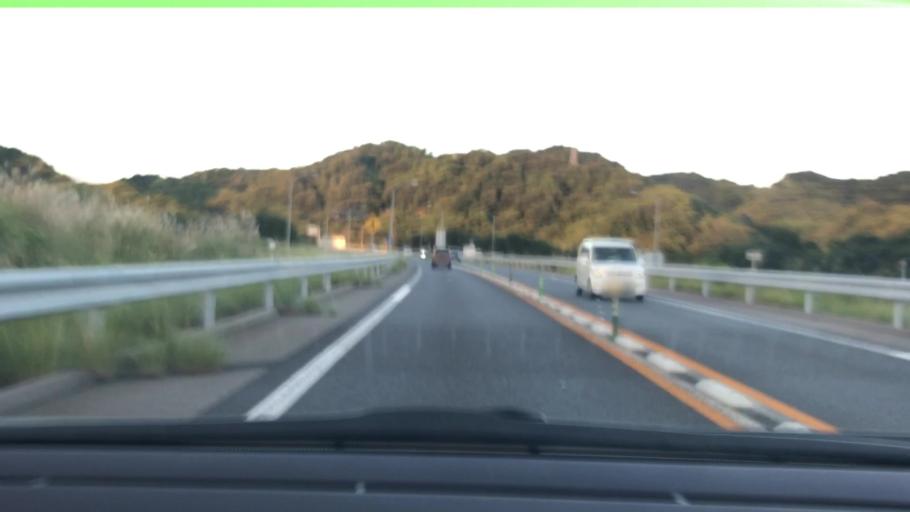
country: JP
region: Hiroshima
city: Innoshima
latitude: 34.3368
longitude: 133.1593
